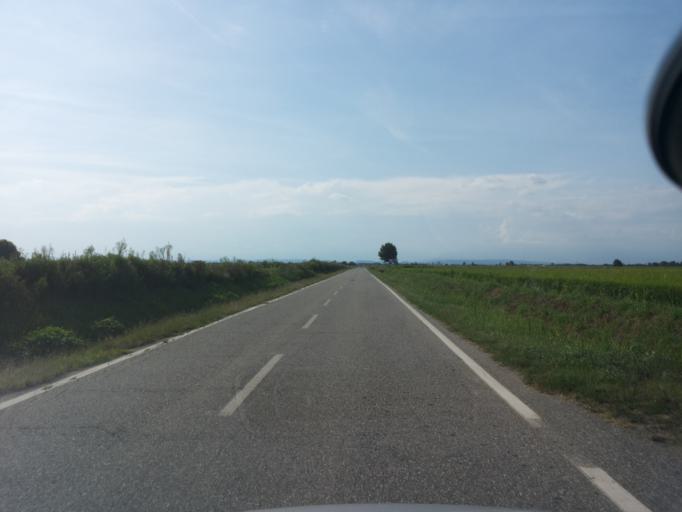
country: IT
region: Piedmont
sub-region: Provincia di Vercelli
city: Salasco
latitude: 45.3027
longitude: 8.2612
